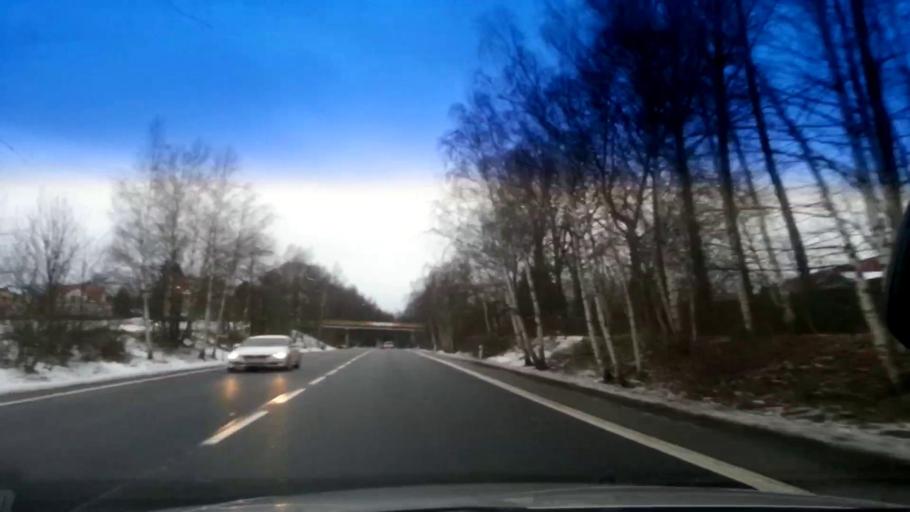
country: CZ
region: Karlovarsky
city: Hazlov
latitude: 50.1543
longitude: 12.2793
